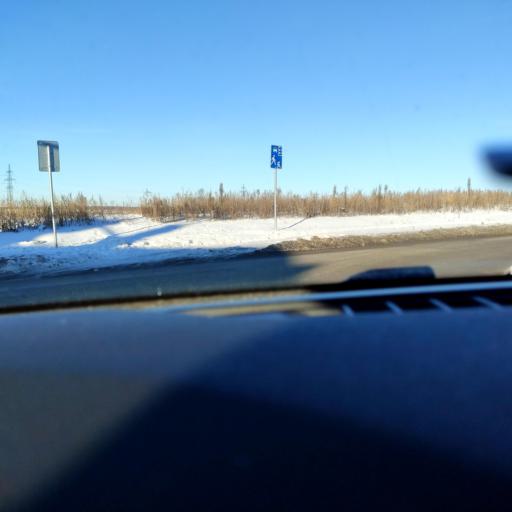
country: RU
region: Samara
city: Petra-Dubrava
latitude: 53.3074
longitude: 50.3432
